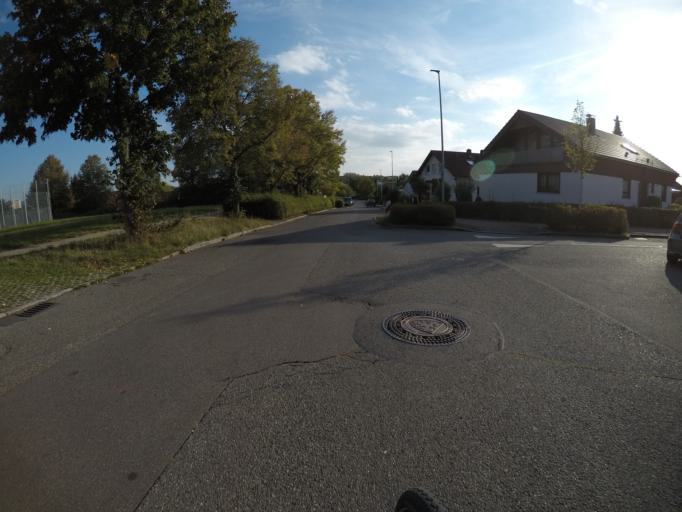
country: DE
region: Baden-Wuerttemberg
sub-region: Tuebingen Region
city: Sickenhausen
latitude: 48.5280
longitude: 9.1976
